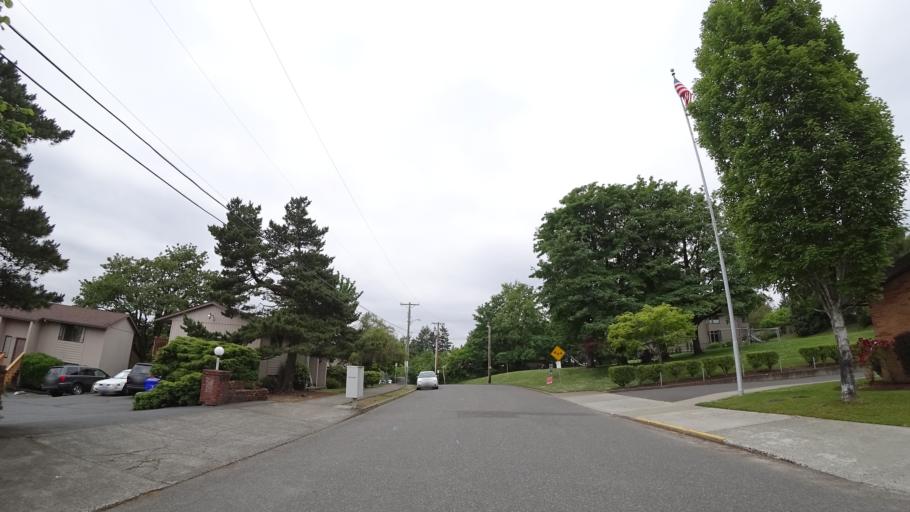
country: US
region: Oregon
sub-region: Multnomah County
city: Portland
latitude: 45.4802
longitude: -122.6934
